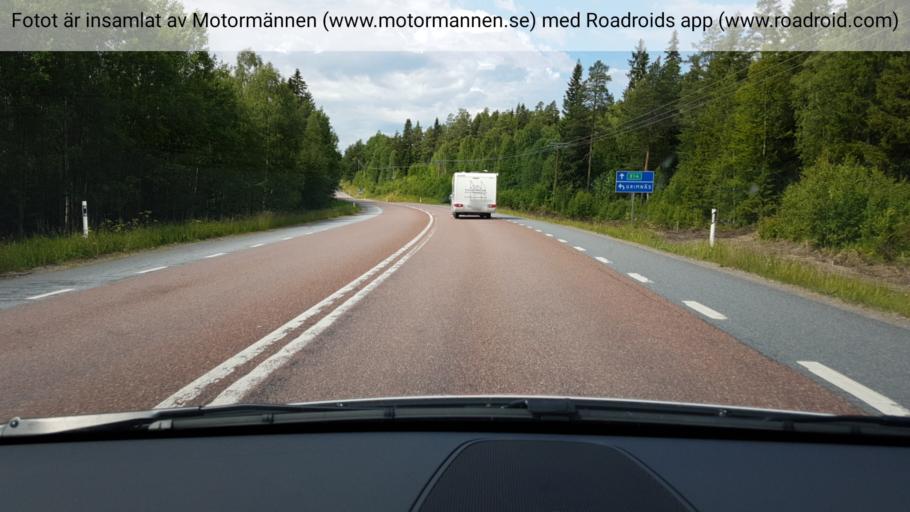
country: SE
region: Jaemtland
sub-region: Braecke Kommun
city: Braecke
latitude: 62.8835
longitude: 15.2766
